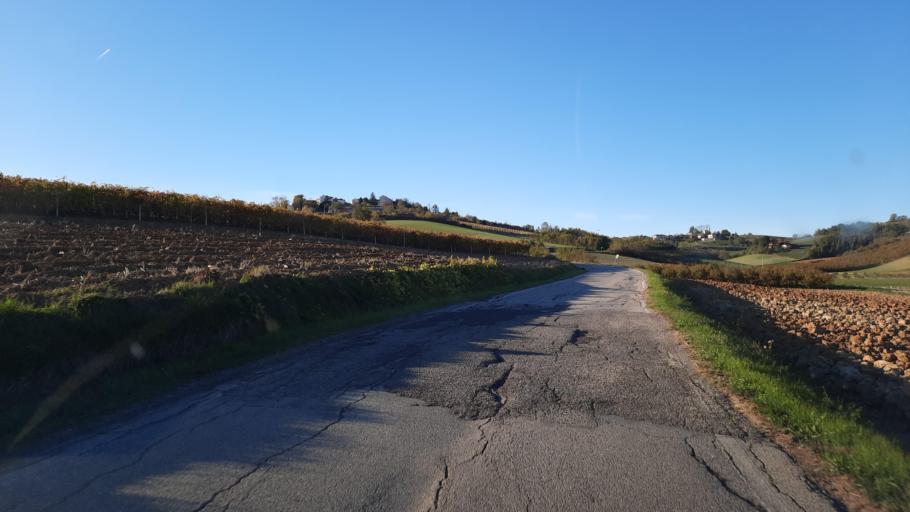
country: IT
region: Piedmont
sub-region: Provincia di Alessandria
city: Cuccaro Monferrato
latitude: 44.9874
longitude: 8.4669
